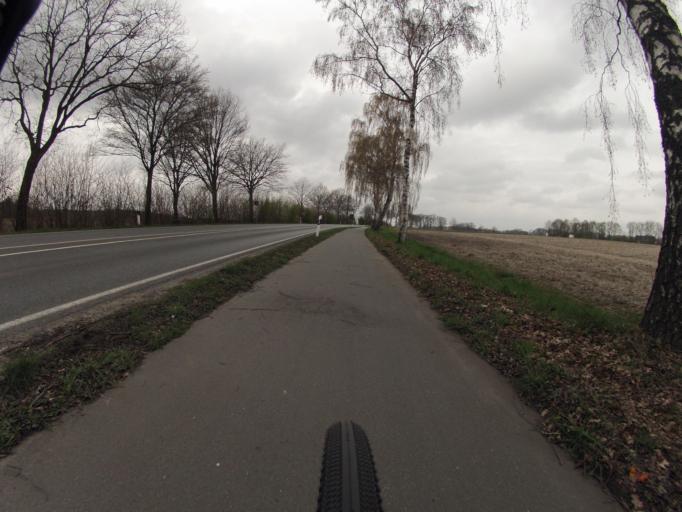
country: DE
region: North Rhine-Westphalia
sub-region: Regierungsbezirk Munster
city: Mettingen
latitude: 52.3241
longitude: 7.7607
